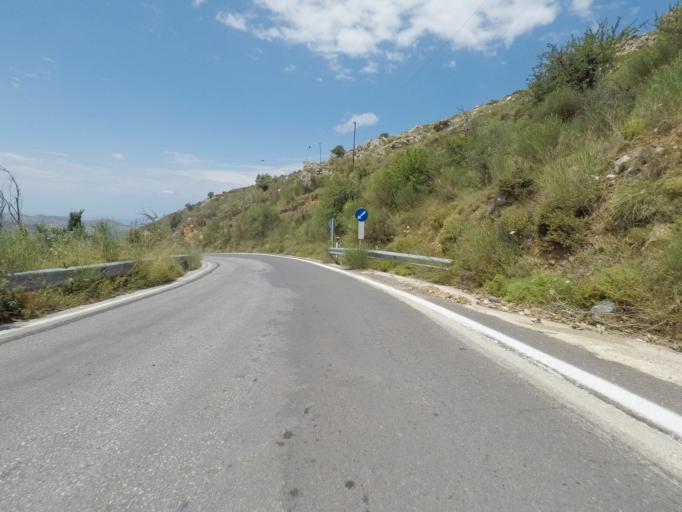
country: GR
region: Crete
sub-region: Nomos Irakleiou
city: Mokhos
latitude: 35.2159
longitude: 25.4593
